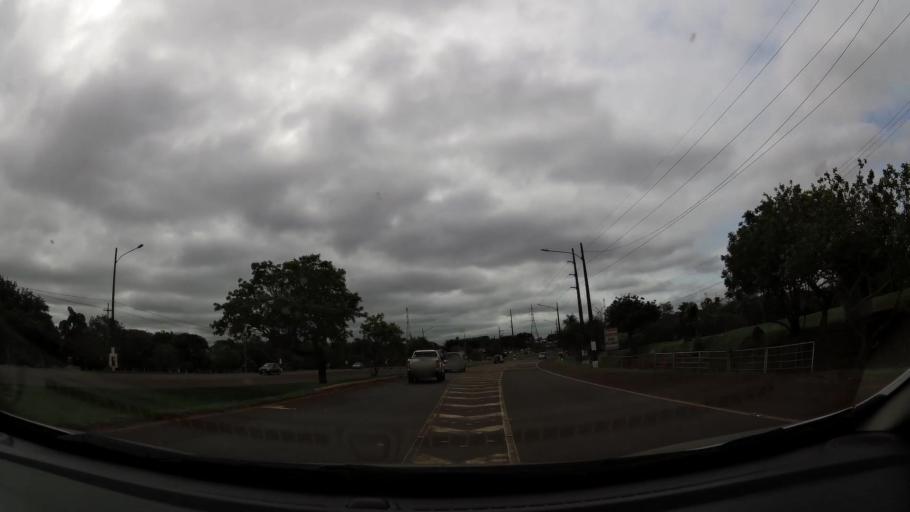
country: PY
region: Alto Parana
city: Ciudad del Este
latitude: -25.4338
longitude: -54.6376
